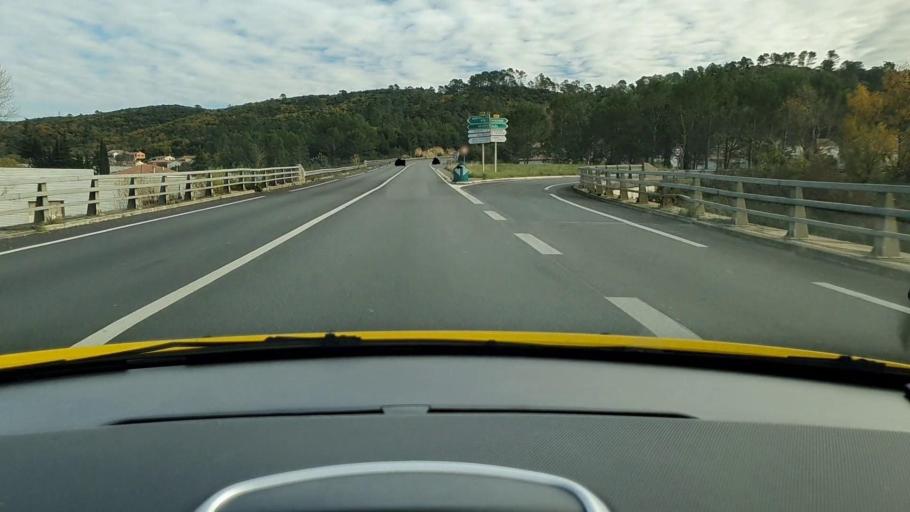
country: FR
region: Languedoc-Roussillon
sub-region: Departement du Gard
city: Saint-Martin-de-Valgalgues
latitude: 44.1580
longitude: 4.0901
